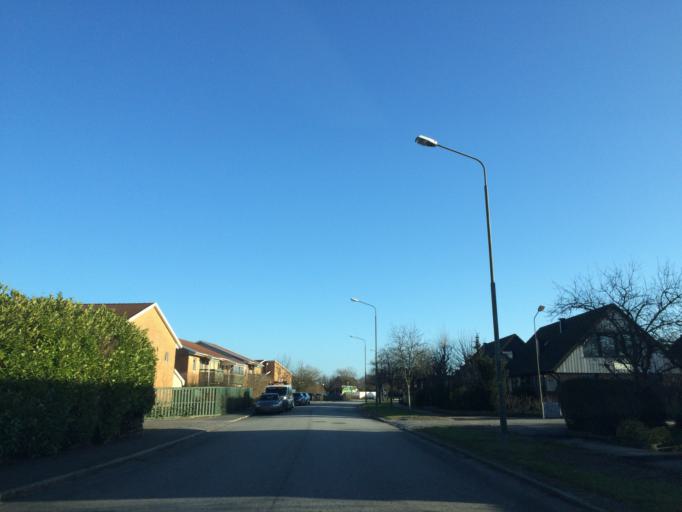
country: SE
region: Skane
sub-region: Malmo
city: Bunkeflostrand
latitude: 55.5726
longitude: 12.9588
